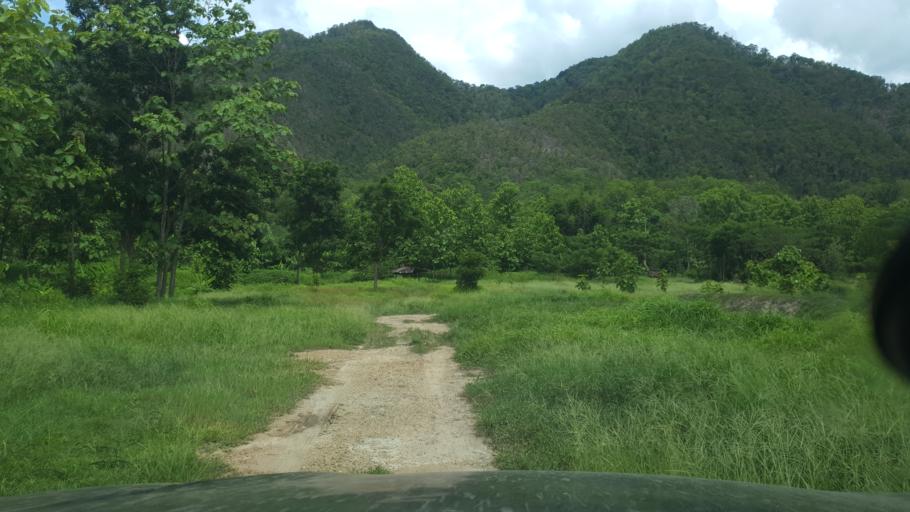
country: TH
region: Lampang
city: Sop Prap
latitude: 17.8536
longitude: 99.3979
